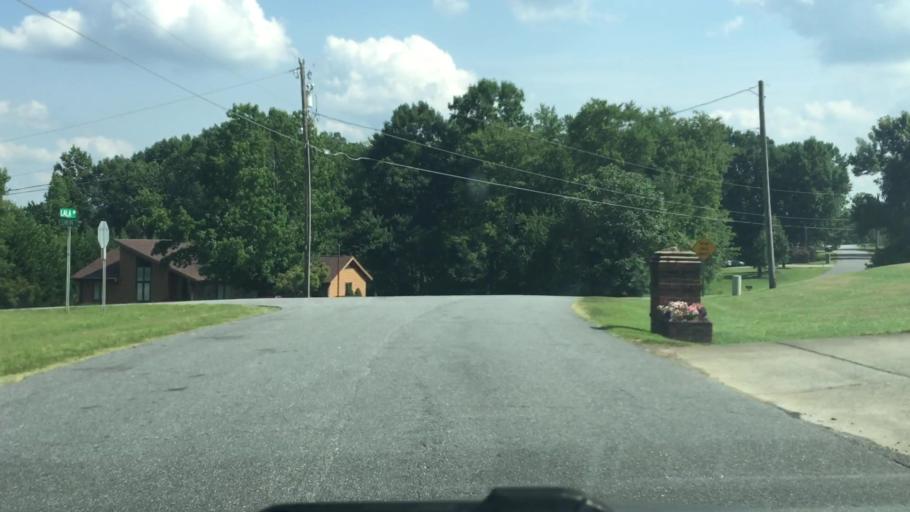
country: US
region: North Carolina
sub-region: Rockingham County
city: Reidsville
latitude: 36.3370
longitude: -79.6124
